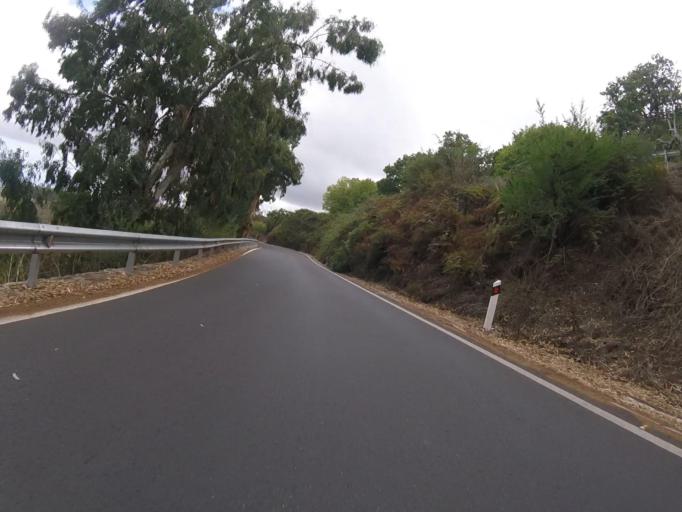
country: ES
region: Canary Islands
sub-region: Provincia de Las Palmas
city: Vega de San Mateo
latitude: 28.0009
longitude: -15.5691
